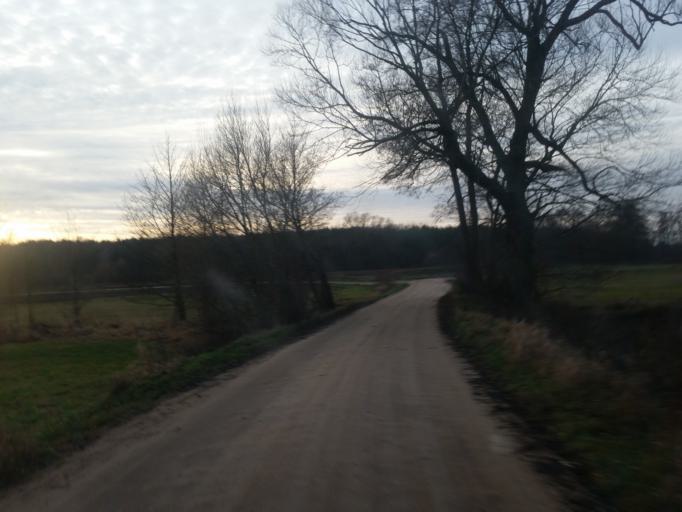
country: PL
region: Kujawsko-Pomorskie
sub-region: Powiat brodnicki
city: Brodnica
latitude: 53.2163
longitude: 19.3356
